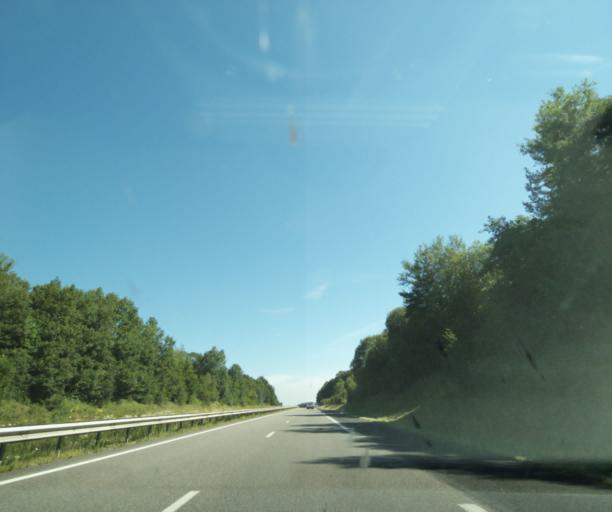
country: FR
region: Lorraine
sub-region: Departement des Vosges
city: Bulgneville
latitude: 48.2463
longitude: 5.8625
